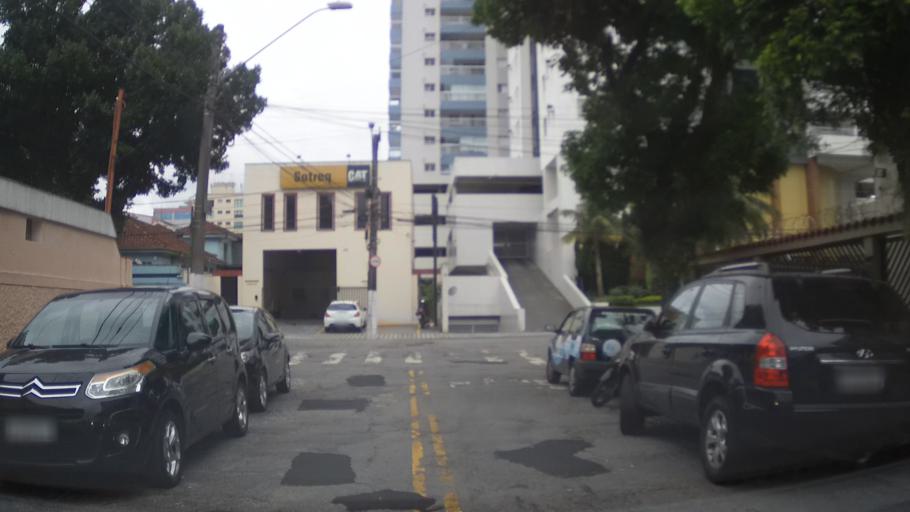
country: BR
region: Sao Paulo
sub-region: Santos
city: Santos
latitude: -23.9572
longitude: -46.3212
